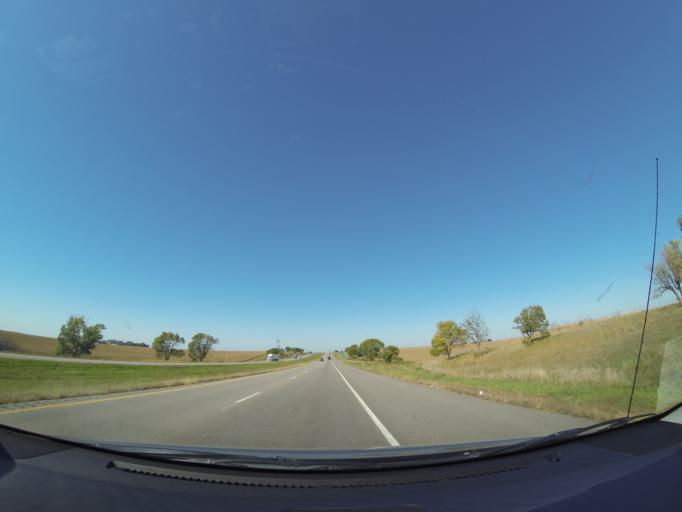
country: US
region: Nebraska
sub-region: Saline County
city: Friend
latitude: 40.8226
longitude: -97.2627
